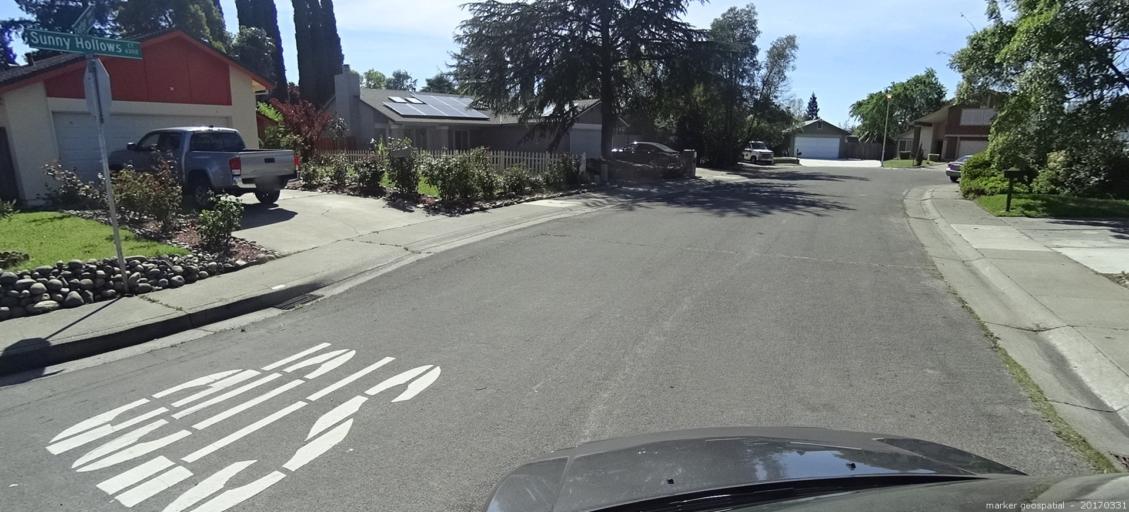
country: US
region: California
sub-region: Sacramento County
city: Laguna
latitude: 38.4556
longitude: -121.4280
